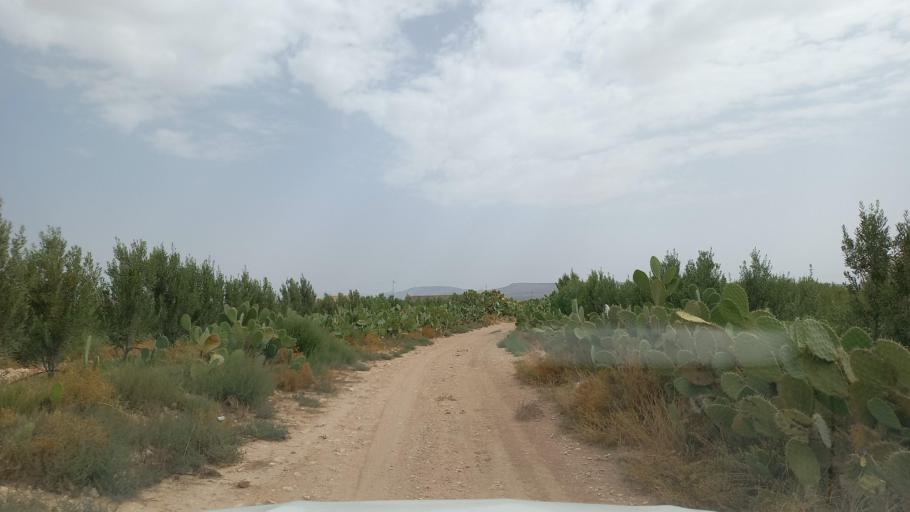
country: TN
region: Al Qasrayn
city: Kasserine
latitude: 35.2825
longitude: 9.0199
